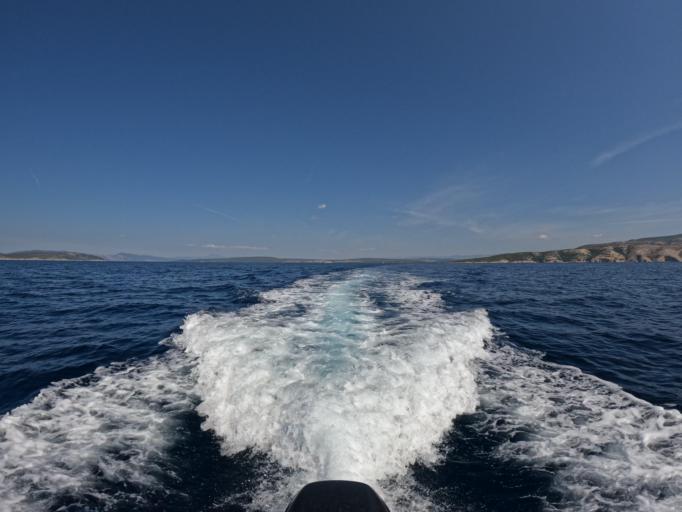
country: HR
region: Primorsko-Goranska
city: Punat
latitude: 44.9500
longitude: 14.6122
